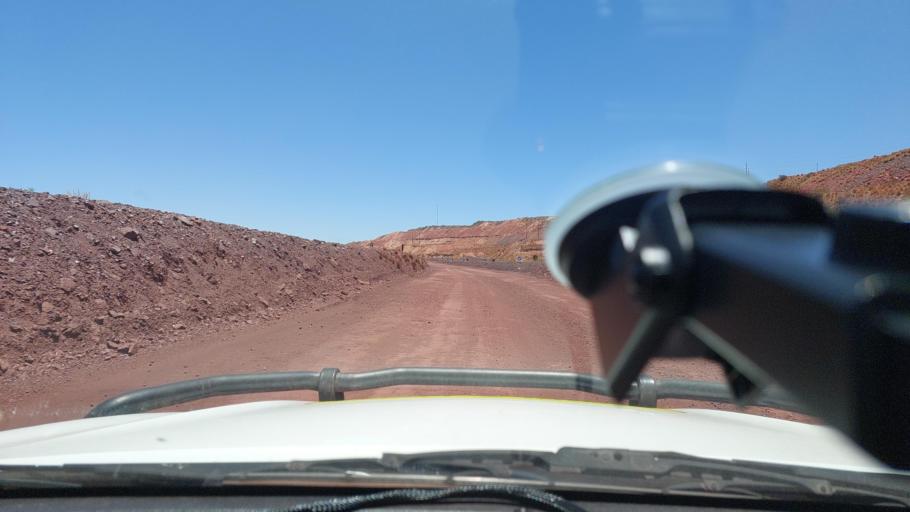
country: ZA
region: Northern Cape
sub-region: John Taolo Gaetsewe District Municipality
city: Kathu
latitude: -27.7186
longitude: 22.9856
